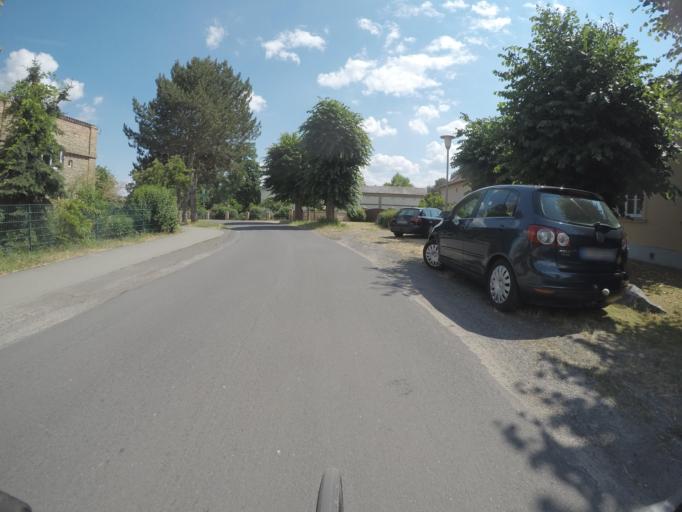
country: DE
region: Brandenburg
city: Roskow
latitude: 52.4410
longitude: 12.7359
